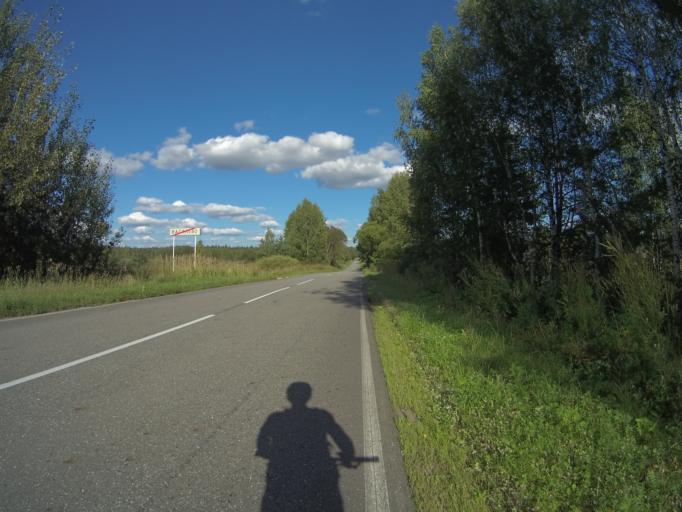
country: RU
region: Vladimir
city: Urshel'skiy
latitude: 55.6079
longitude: 40.2591
